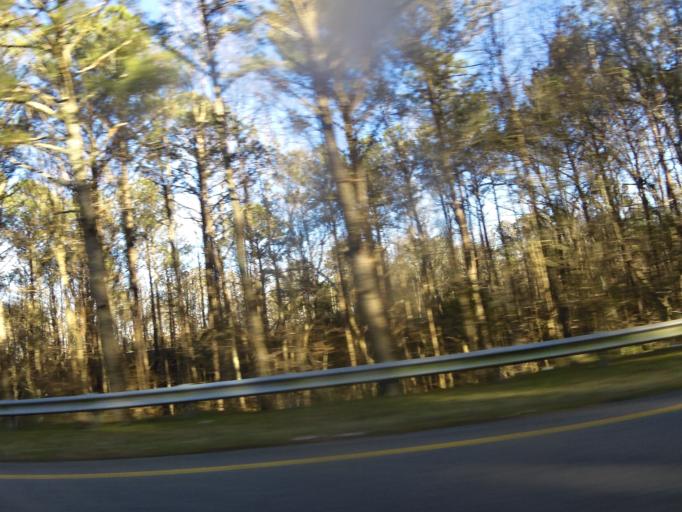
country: US
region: Virginia
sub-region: Isle of Wight County
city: Windsor
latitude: 36.6813
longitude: -76.7728
